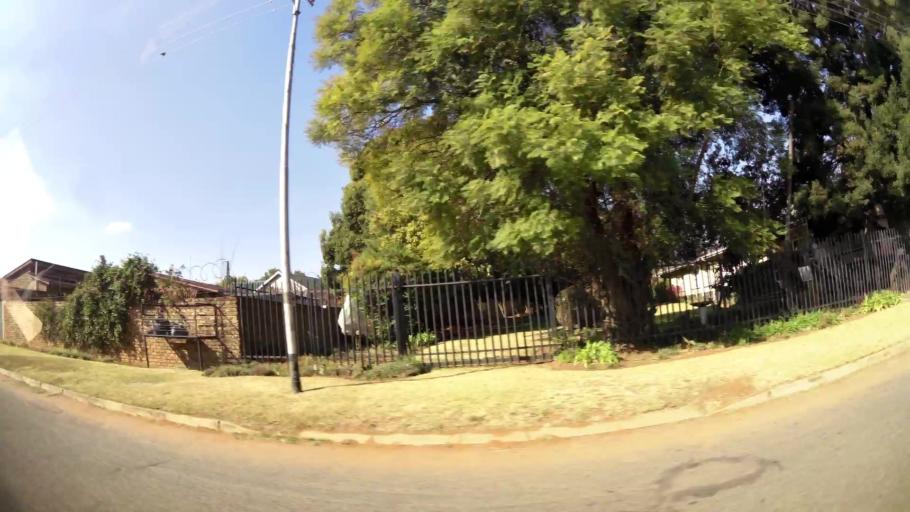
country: ZA
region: Gauteng
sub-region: West Rand District Municipality
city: Randfontein
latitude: -26.1504
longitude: 27.7014
